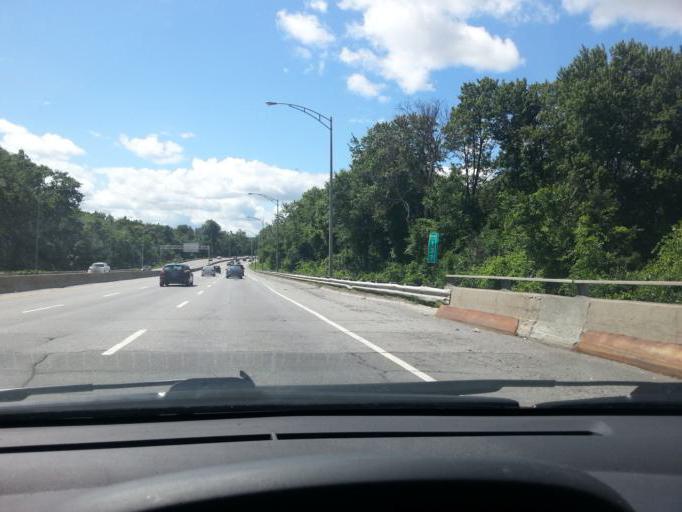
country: CA
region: Quebec
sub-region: Outaouais
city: Gatineau
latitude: 45.4546
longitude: -75.7161
